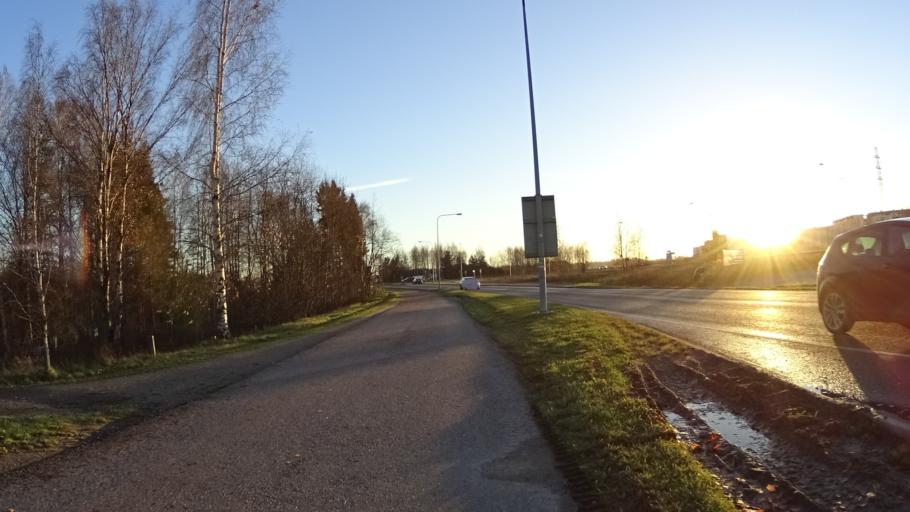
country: FI
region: Uusimaa
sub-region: Helsinki
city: Vantaa
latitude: 60.2704
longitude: 24.9750
